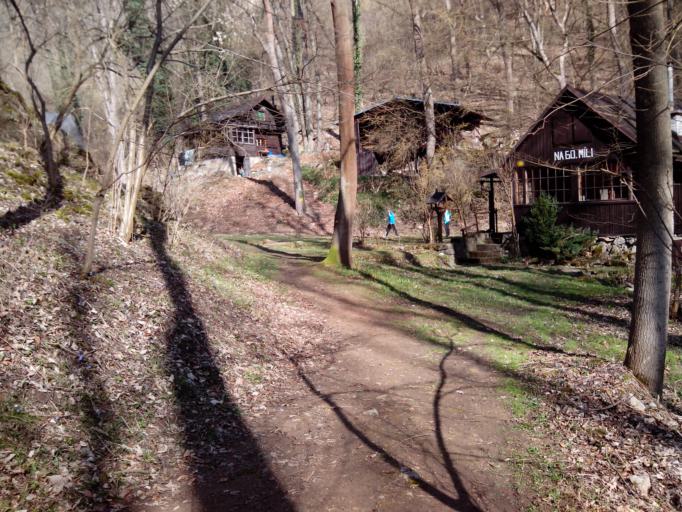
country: CZ
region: Central Bohemia
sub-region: Okres Beroun
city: Beroun
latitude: 49.9324
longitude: 14.1240
